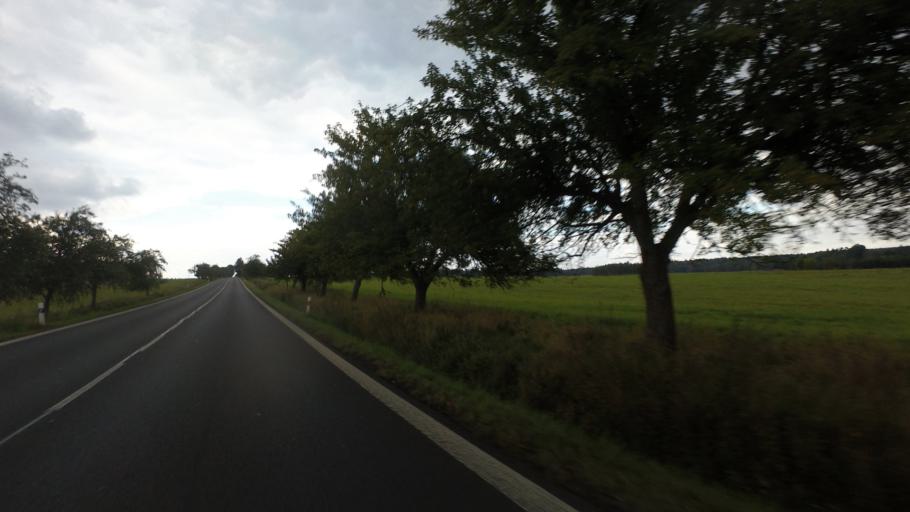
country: CZ
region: Ustecky
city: Stare Krecany
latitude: 50.9664
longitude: 14.5258
